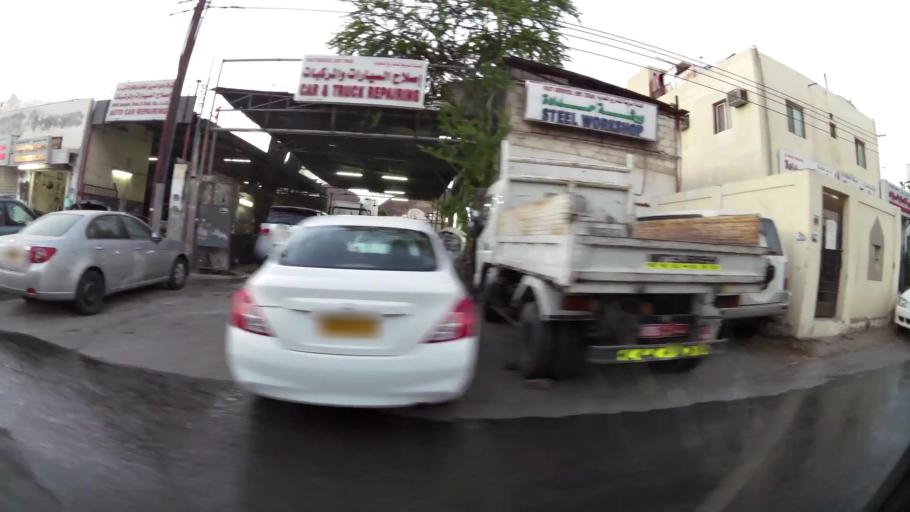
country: OM
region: Muhafazat Masqat
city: Muscat
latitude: 23.5917
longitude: 58.5651
